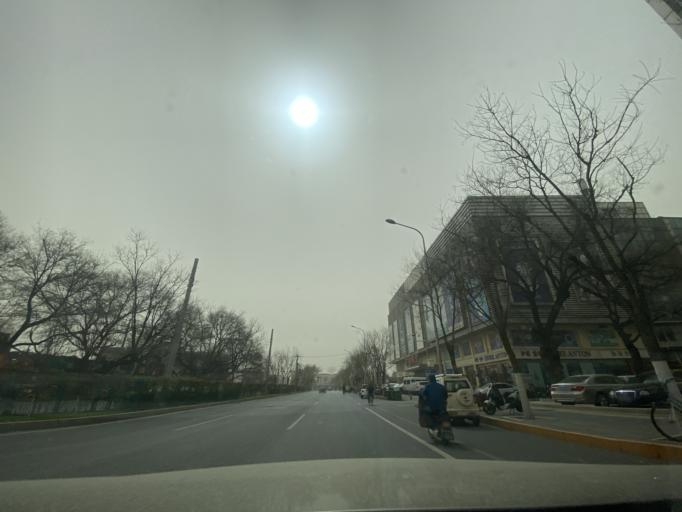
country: CN
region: Beijing
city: Jinrongjie
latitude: 39.9419
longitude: 116.3660
